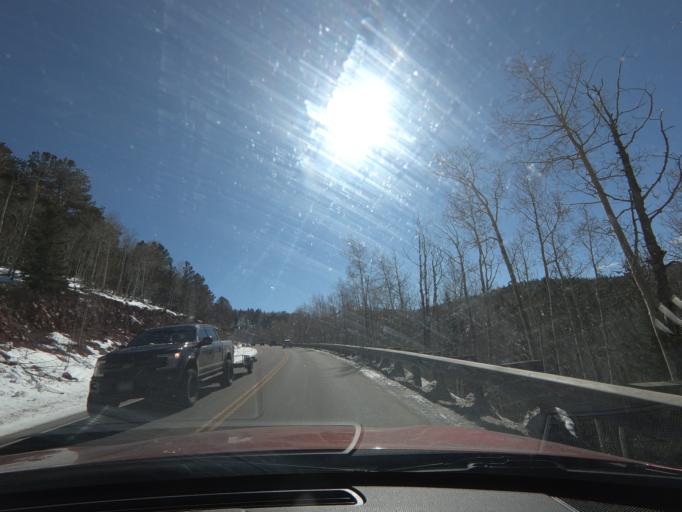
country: US
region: Colorado
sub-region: Teller County
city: Cripple Creek
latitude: 38.8067
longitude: -105.1239
